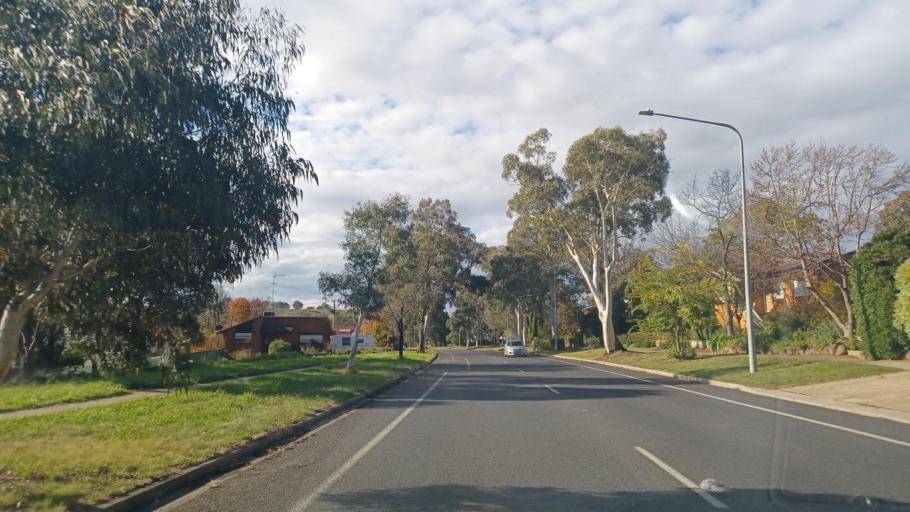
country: AU
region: Australian Capital Territory
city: Belconnen
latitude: -35.1911
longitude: 149.0451
